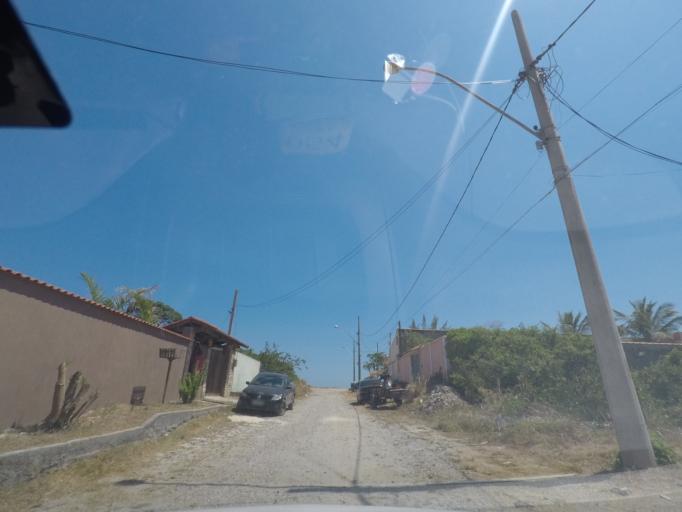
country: BR
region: Rio de Janeiro
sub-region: Marica
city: Marica
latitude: -22.9733
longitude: -42.9243
